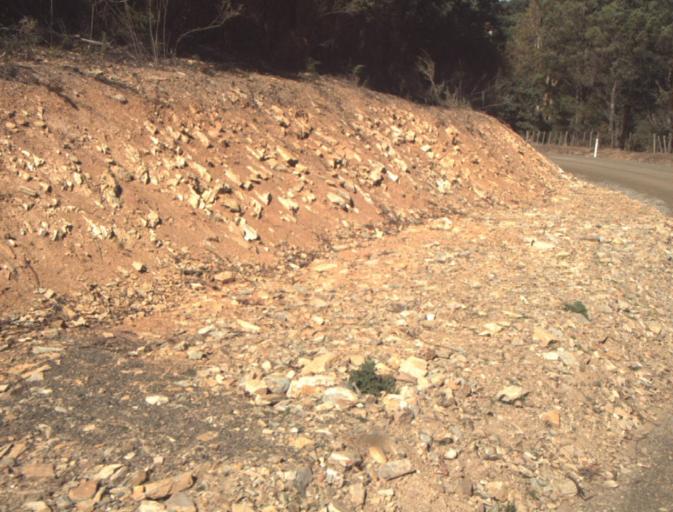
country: AU
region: Tasmania
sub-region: Launceston
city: Newstead
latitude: -41.2954
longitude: 147.3384
